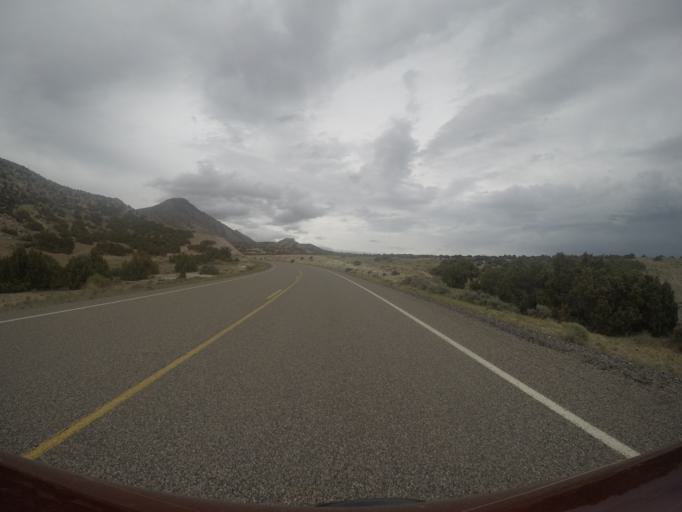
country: US
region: Wyoming
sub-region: Big Horn County
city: Lovell
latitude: 45.0150
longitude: -108.2667
